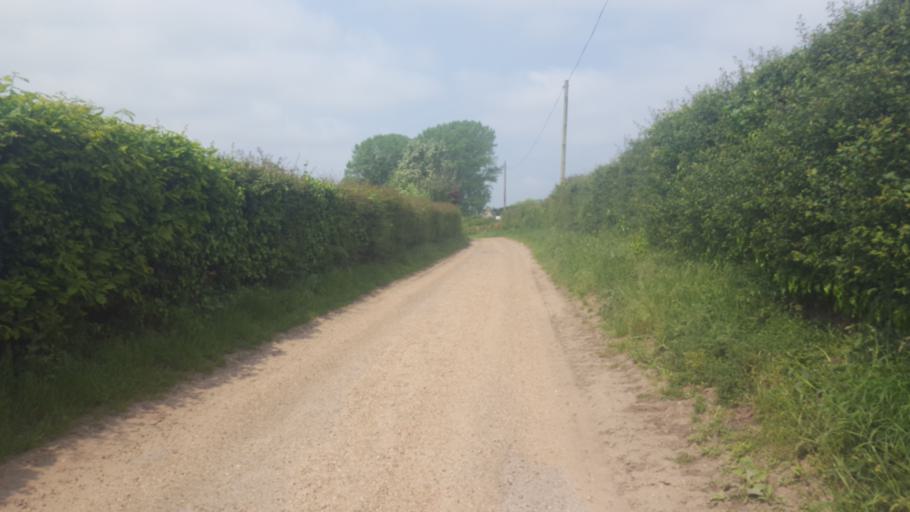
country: GB
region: England
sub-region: Essex
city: Saint Osyth
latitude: 51.7982
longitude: 1.0996
